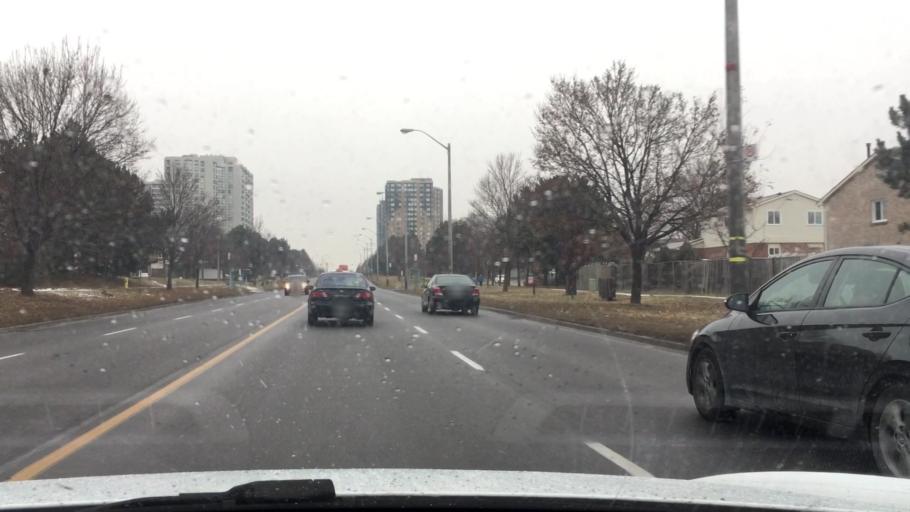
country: CA
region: Ontario
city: Markham
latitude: 43.8192
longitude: -79.2725
